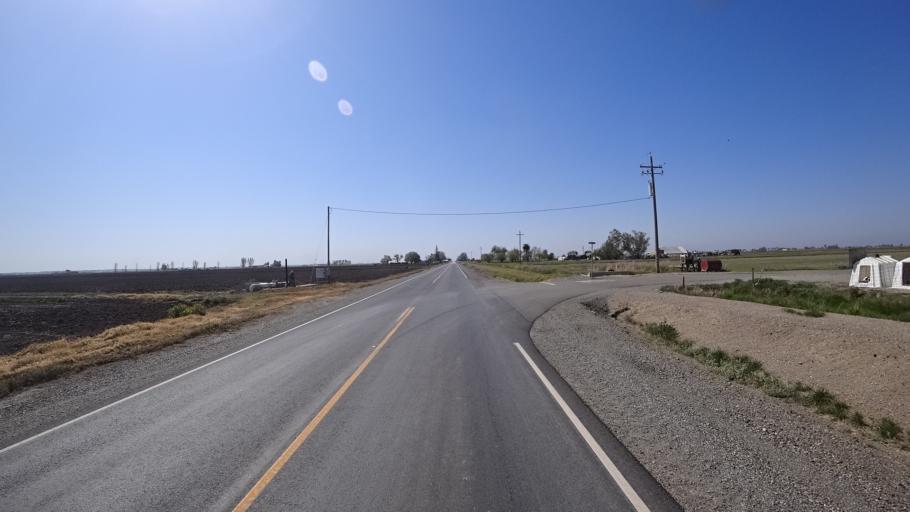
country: US
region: California
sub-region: Glenn County
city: Willows
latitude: 39.5729
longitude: -122.0653
